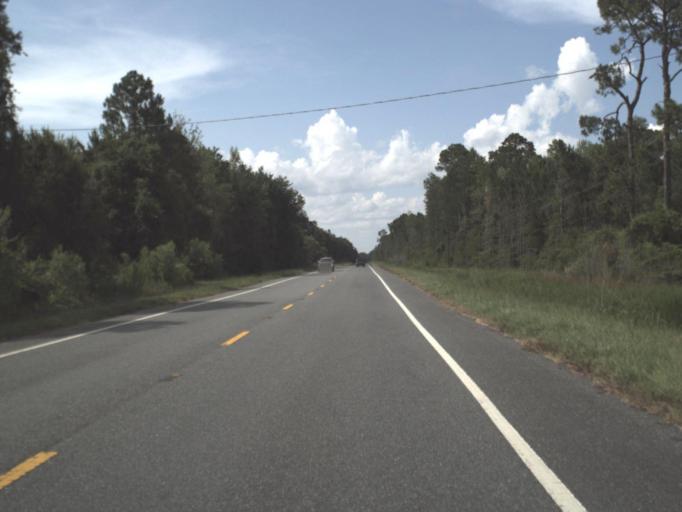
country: US
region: Florida
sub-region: Taylor County
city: Perry
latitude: 30.2599
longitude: -83.6250
